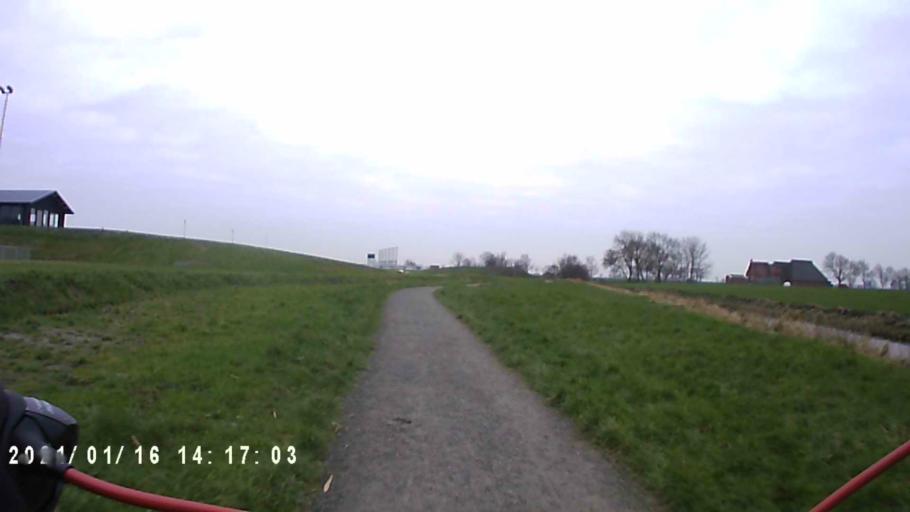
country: NL
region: Groningen
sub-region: Gemeente Winsum
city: Winsum
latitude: 53.3273
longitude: 6.5085
